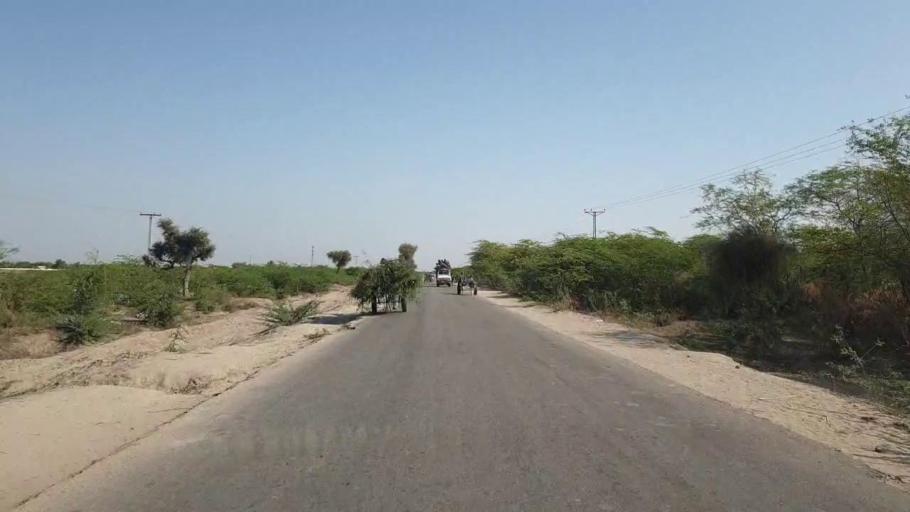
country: PK
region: Sindh
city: Chor
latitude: 25.4617
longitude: 69.7640
